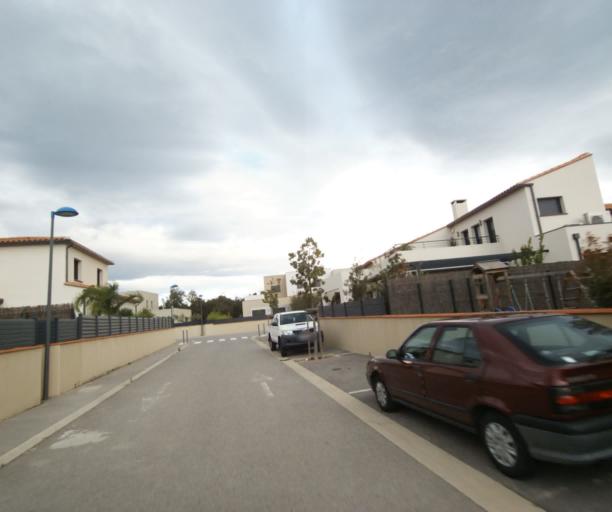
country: FR
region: Languedoc-Roussillon
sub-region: Departement des Pyrenees-Orientales
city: Argelers
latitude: 42.5562
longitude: 3.0217
